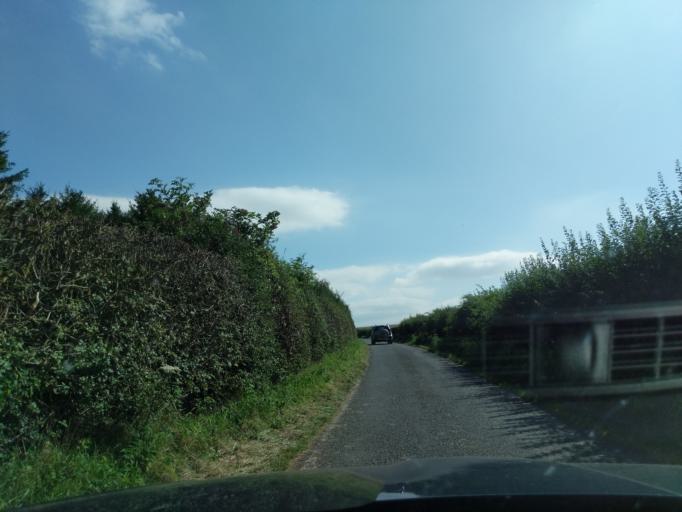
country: GB
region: Scotland
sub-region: The Scottish Borders
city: Coldstream
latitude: 55.6683
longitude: -2.1655
